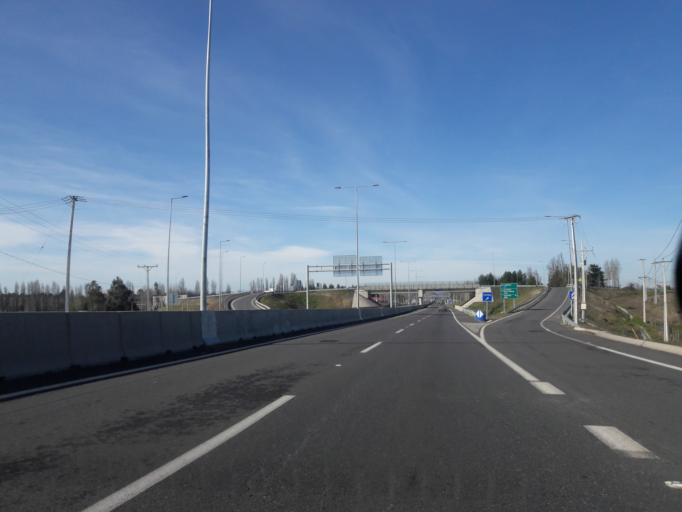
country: CL
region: Biobio
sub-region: Provincia de Biobio
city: Yumbel
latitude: -37.0017
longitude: -72.5445
